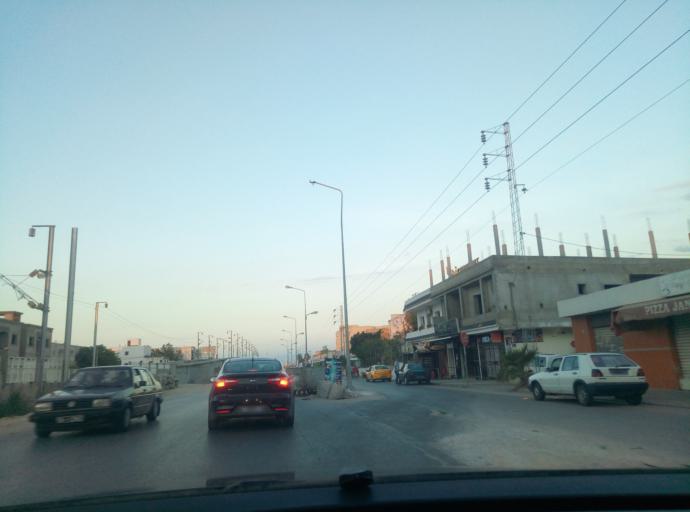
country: TN
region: Manouba
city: Manouba
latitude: 36.7812
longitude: 10.1074
